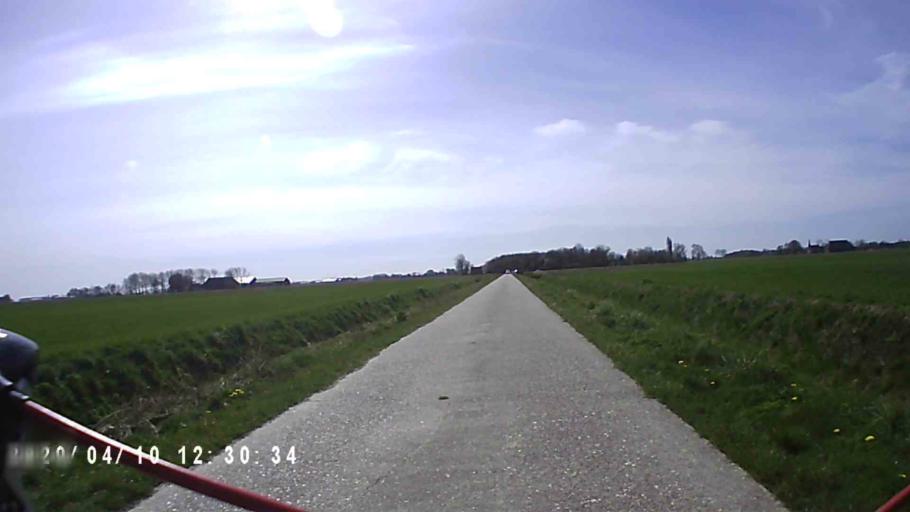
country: NL
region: Groningen
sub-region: Gemeente De Marne
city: Ulrum
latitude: 53.4001
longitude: 6.4099
